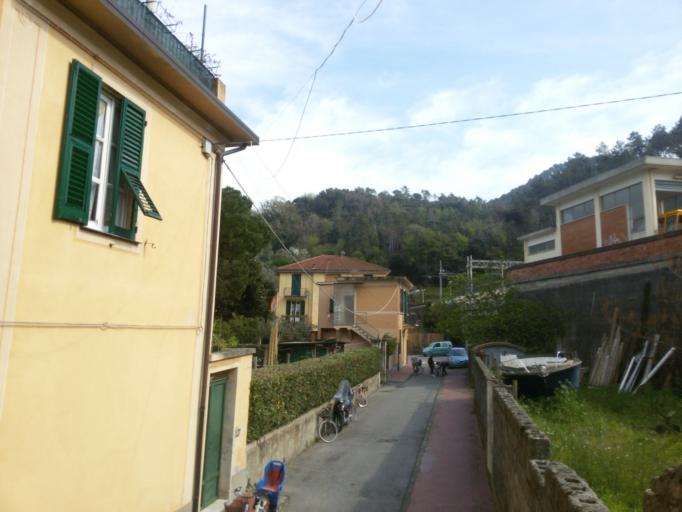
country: IT
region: Liguria
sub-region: Provincia di La Spezia
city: Levanto
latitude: 44.1738
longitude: 9.6179
